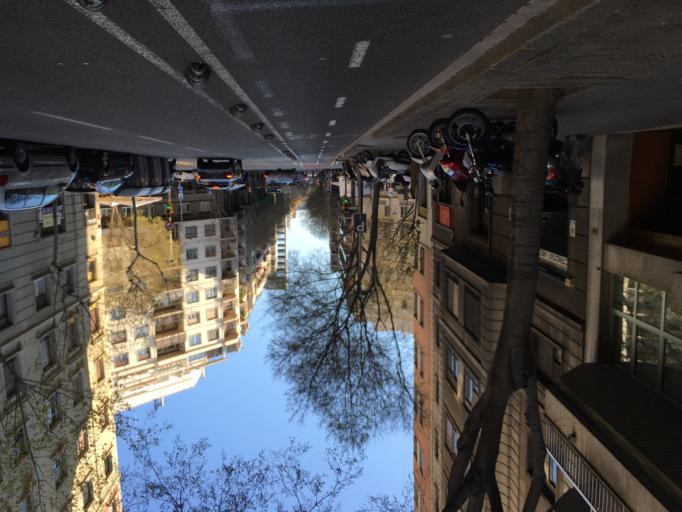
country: ES
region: Catalonia
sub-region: Provincia de Barcelona
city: Sants-Montjuic
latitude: 41.3818
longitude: 2.1522
